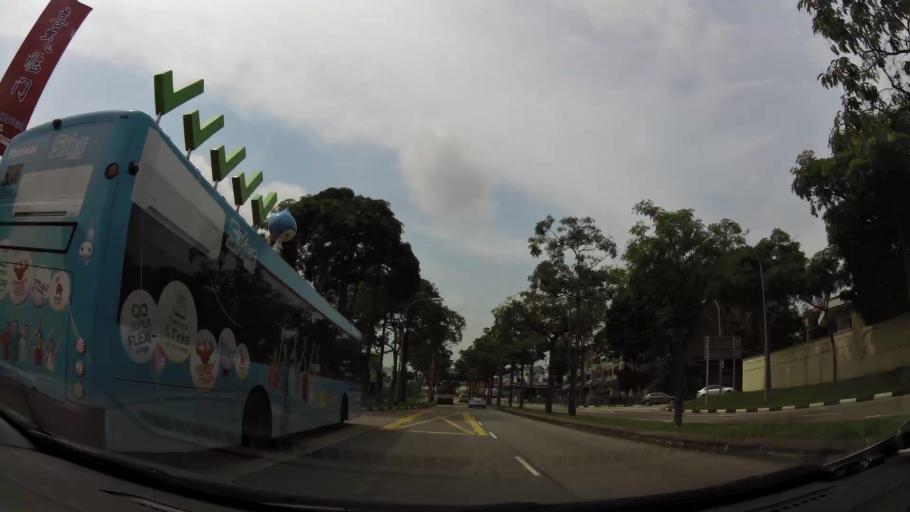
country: SG
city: Singapore
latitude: 1.3608
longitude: 103.9710
